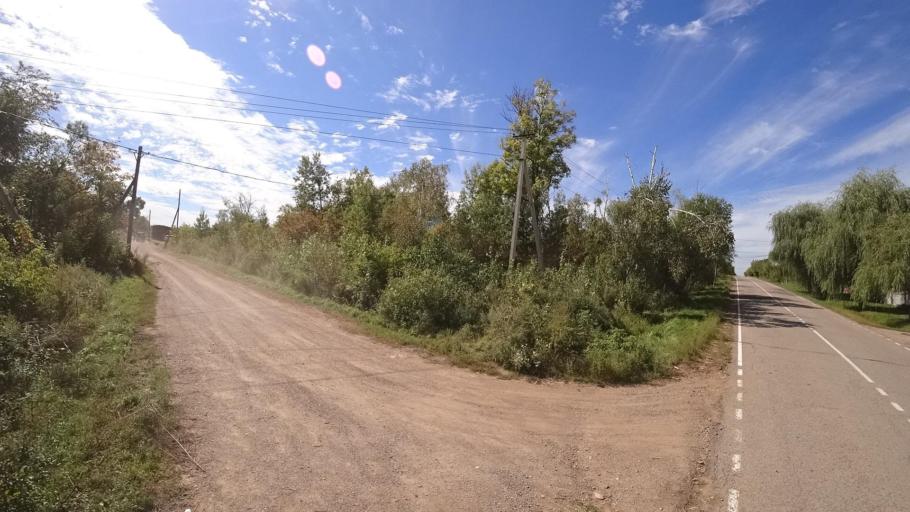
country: RU
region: Primorskiy
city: Yakovlevka
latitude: 44.4308
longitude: 133.5667
